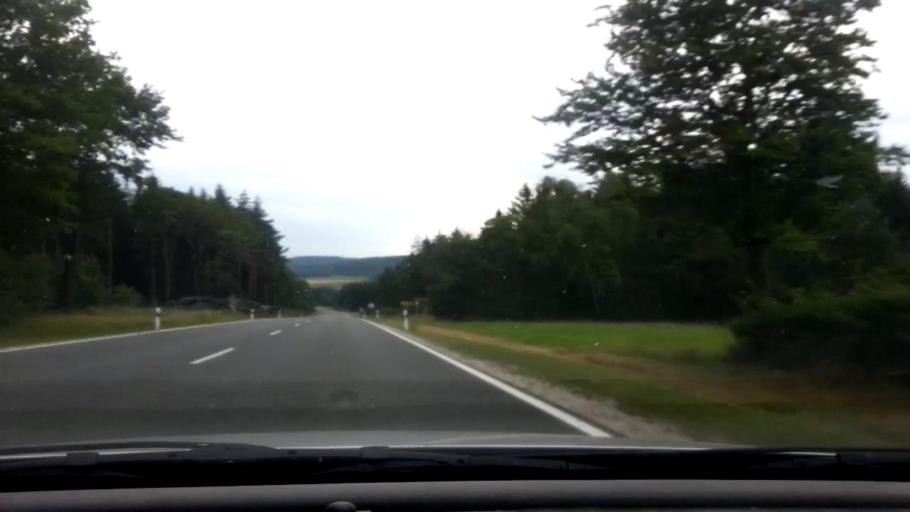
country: DE
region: Bavaria
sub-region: Upper Palatinate
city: Erbendorf
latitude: 49.8449
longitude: 12.0004
